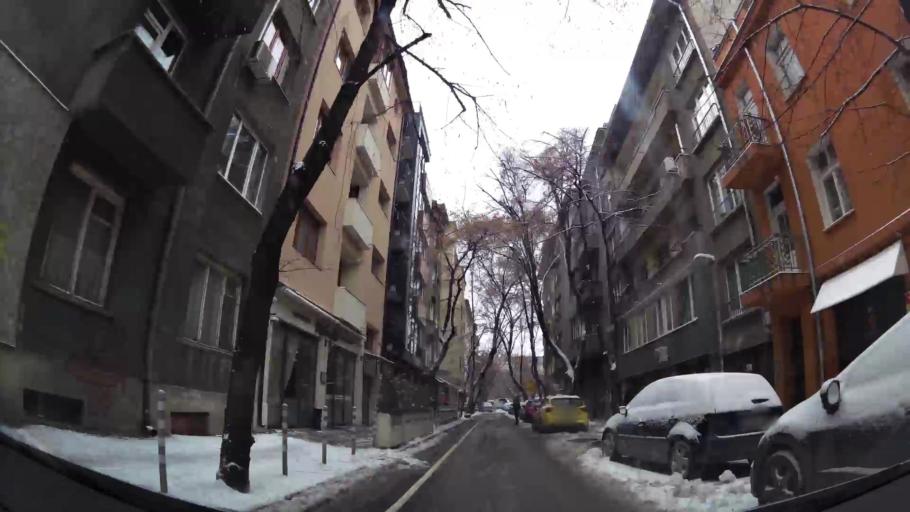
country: BG
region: Sofia-Capital
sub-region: Stolichna Obshtina
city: Sofia
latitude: 42.6906
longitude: 23.3169
